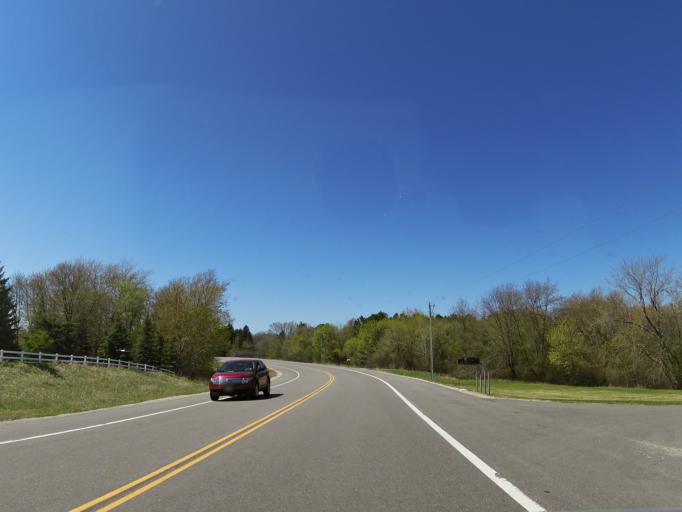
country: US
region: Minnesota
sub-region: Scott County
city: Prior Lake
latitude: 44.7601
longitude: -93.3929
